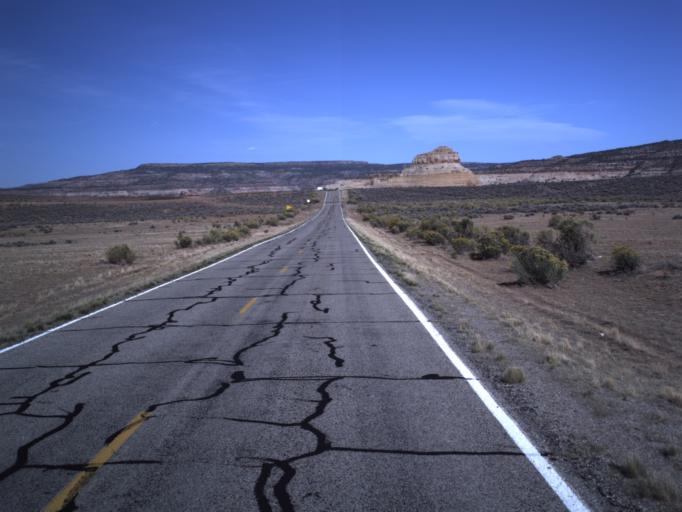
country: US
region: Utah
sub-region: San Juan County
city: Monticello
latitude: 38.0713
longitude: -109.3610
